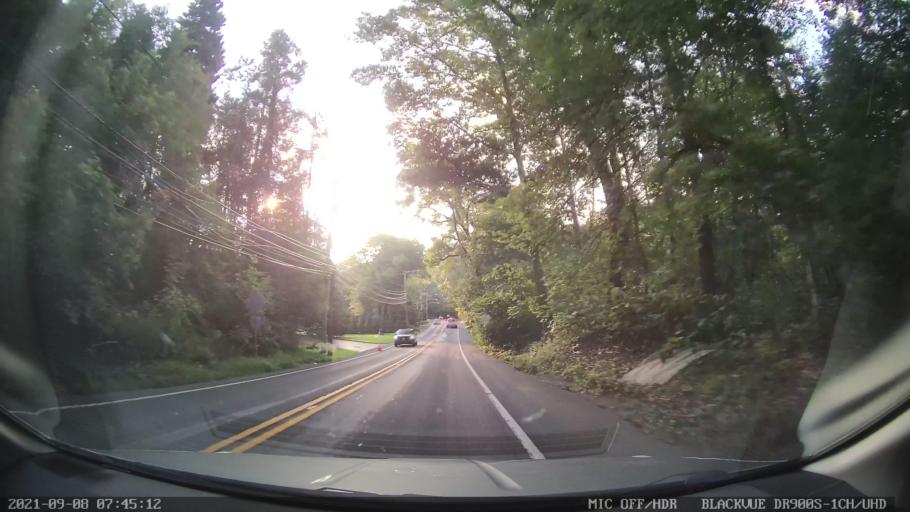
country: US
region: Pennsylvania
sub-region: Delaware County
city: Radnor
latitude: 40.0581
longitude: -75.3705
